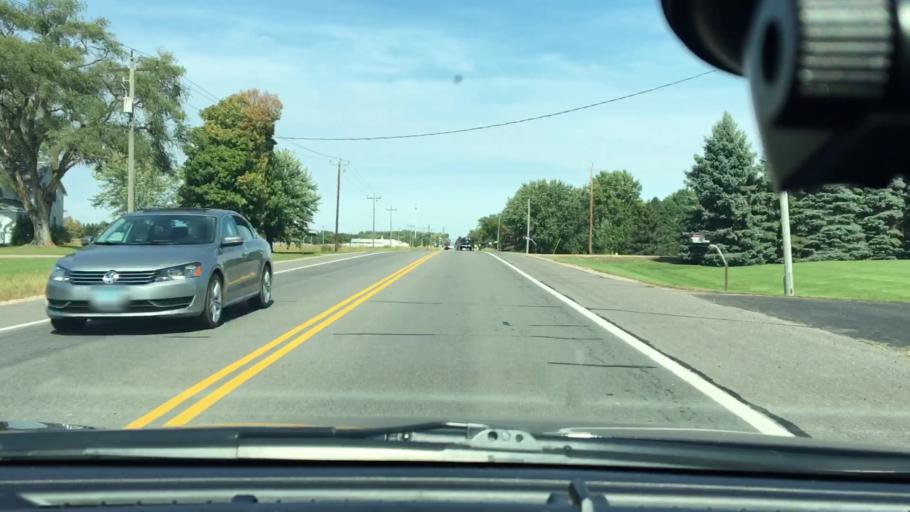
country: US
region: Minnesota
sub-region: Wright County
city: Saint Michael
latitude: 45.1917
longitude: -93.6651
